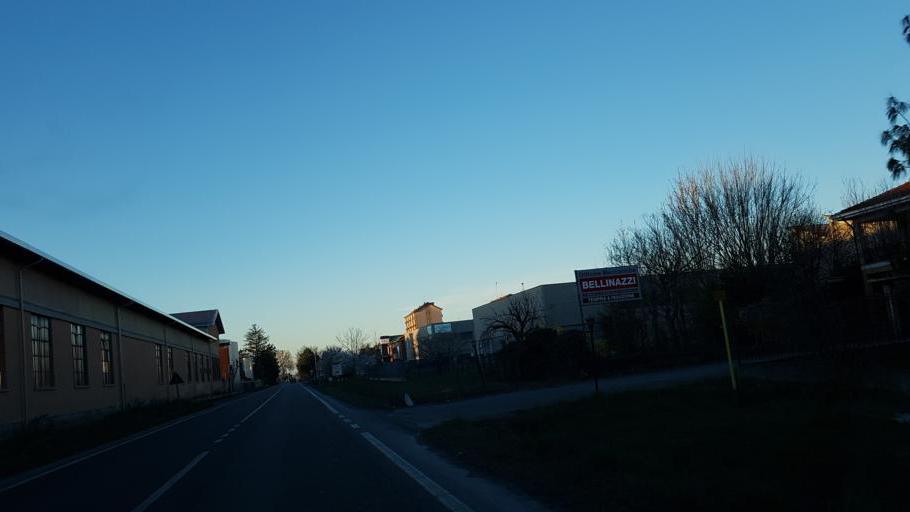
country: IT
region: Piedmont
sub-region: Provincia di Alessandria
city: Carbonara Scrivia
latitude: 44.8579
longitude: 8.8549
